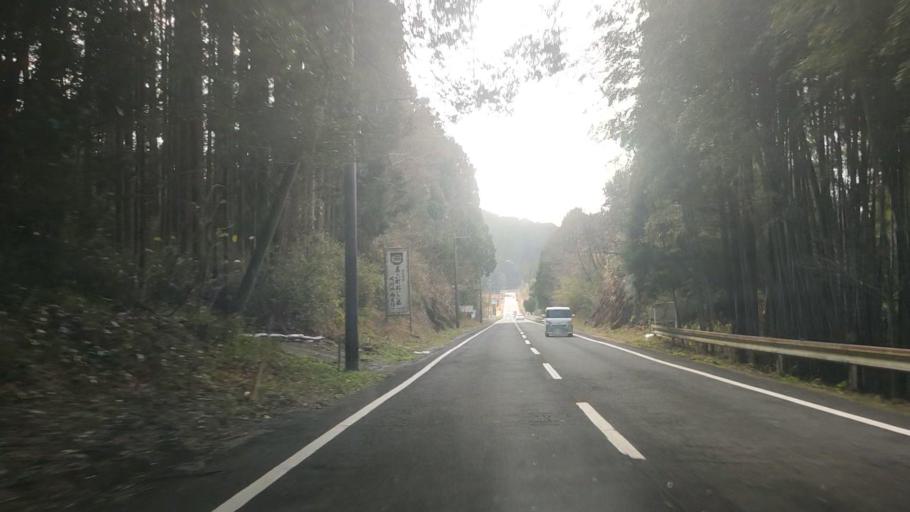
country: JP
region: Kagoshima
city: Okuchi-shinohara
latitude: 31.9665
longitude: 130.7394
